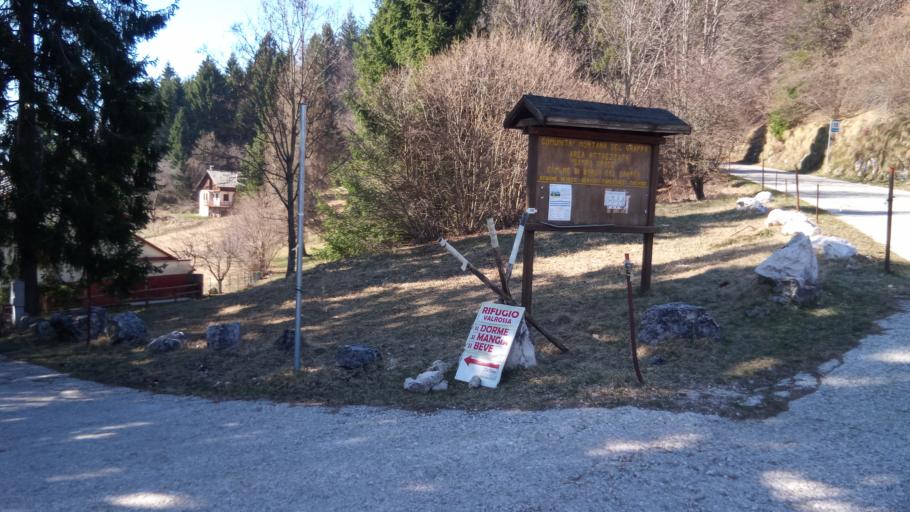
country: IT
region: Veneto
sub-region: Provincia di Treviso
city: Borso del Grappa
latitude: 45.8368
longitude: 11.7808
